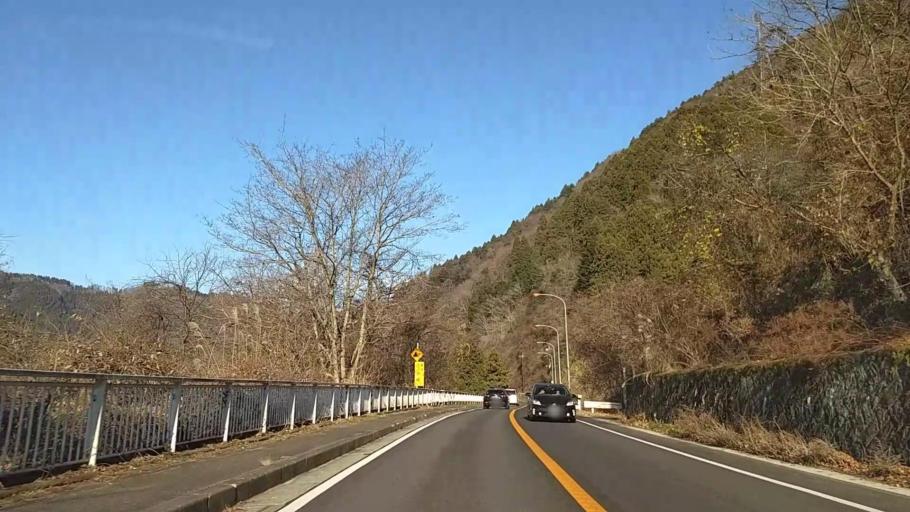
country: JP
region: Tokyo
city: Hachioji
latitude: 35.5327
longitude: 139.2400
